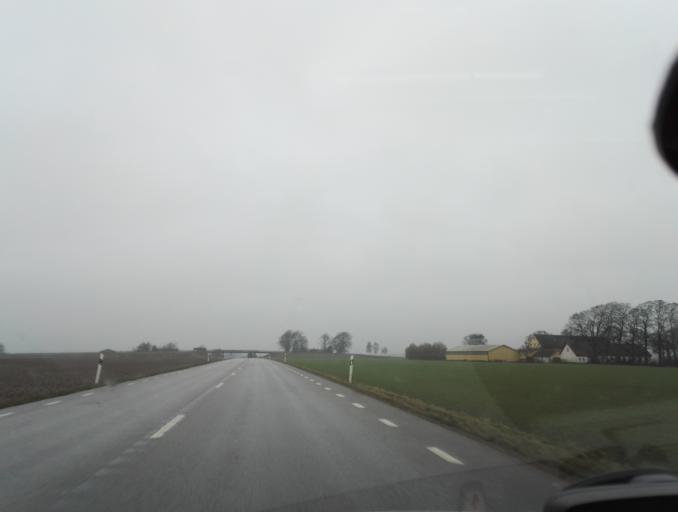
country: SE
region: Skane
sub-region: Kavlinge Kommun
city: Kaevlinge
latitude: 55.7819
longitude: 13.1337
